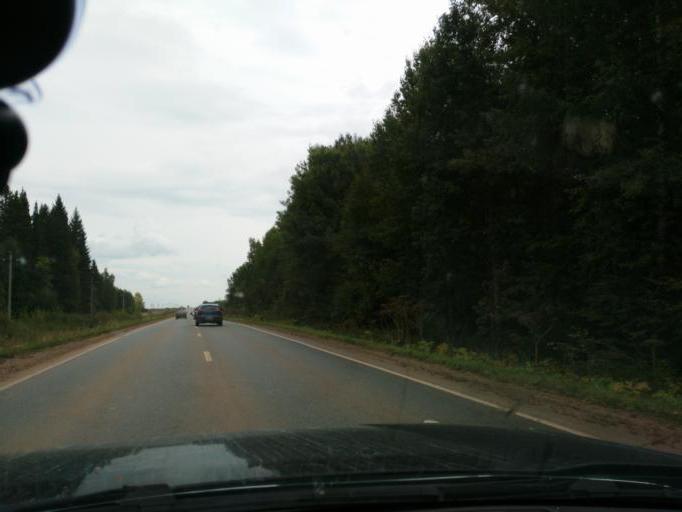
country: RU
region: Perm
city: Chernushka
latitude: 56.5101
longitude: 55.9400
